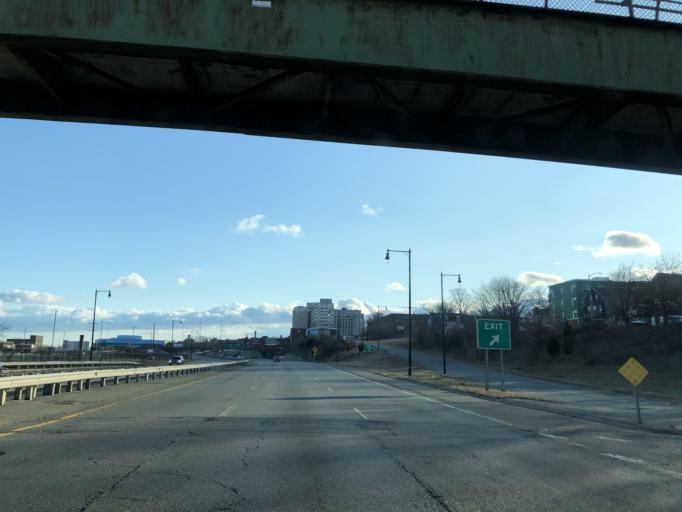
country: US
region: Massachusetts
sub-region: Bristol County
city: New Bedford
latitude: 41.6446
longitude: -70.9270
